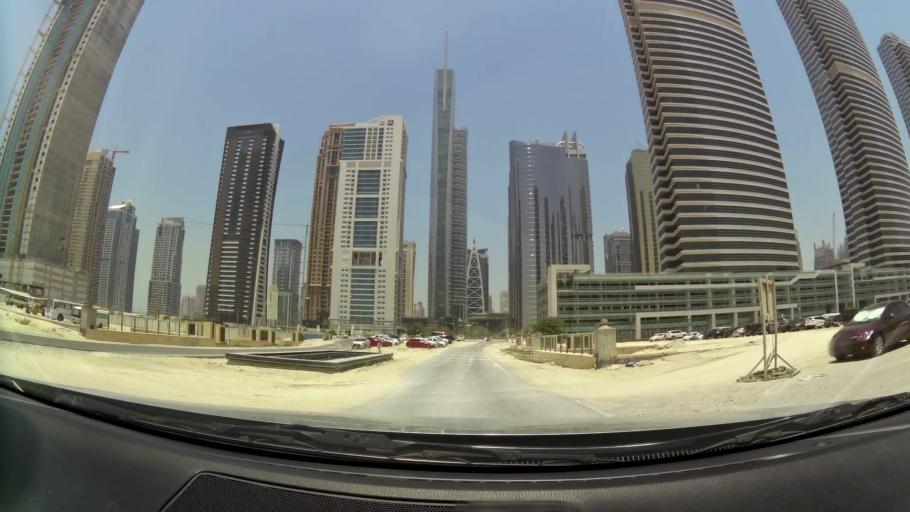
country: AE
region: Dubai
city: Dubai
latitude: 25.0661
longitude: 55.1446
